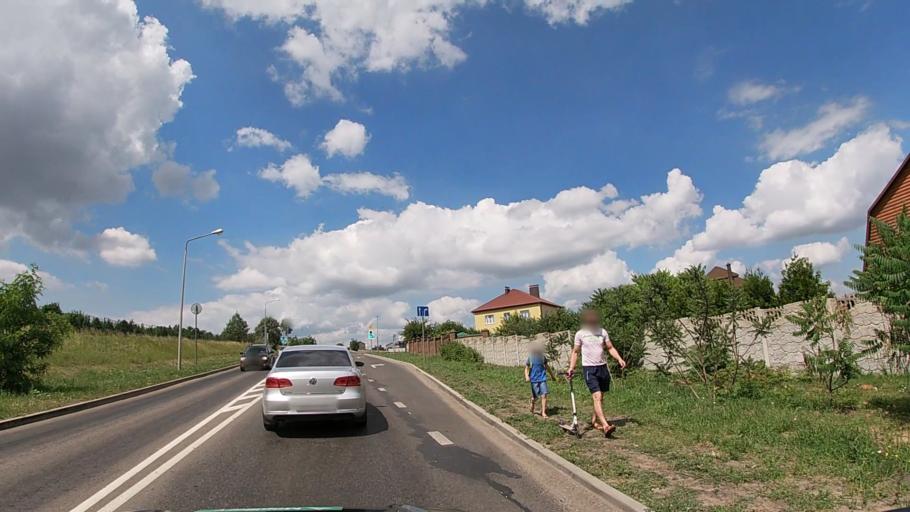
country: RU
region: Belgorod
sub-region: Belgorodskiy Rayon
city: Belgorod
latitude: 50.5949
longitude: 36.5429
